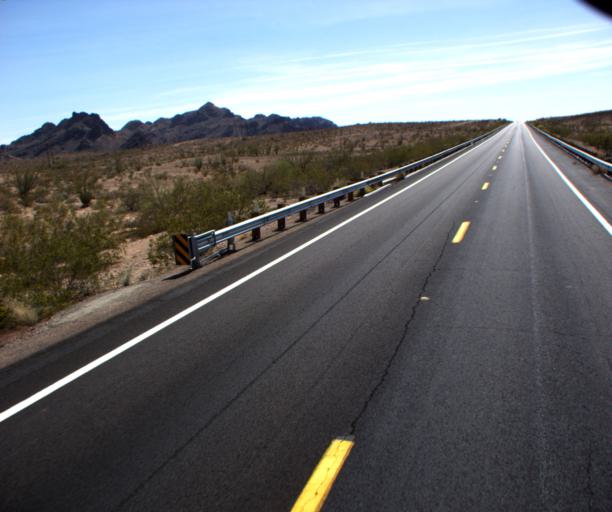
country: US
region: Arizona
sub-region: La Paz County
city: Quartzsite
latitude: 33.2509
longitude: -114.2471
